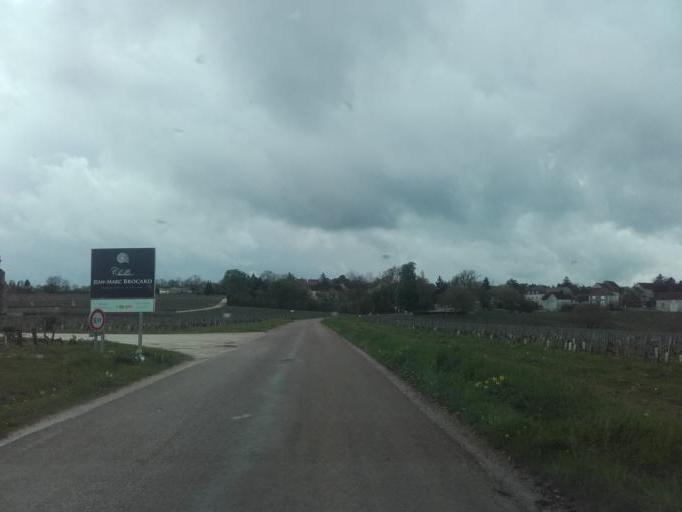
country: FR
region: Bourgogne
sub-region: Departement de l'Yonne
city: Chablis
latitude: 47.7625
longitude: 3.7618
